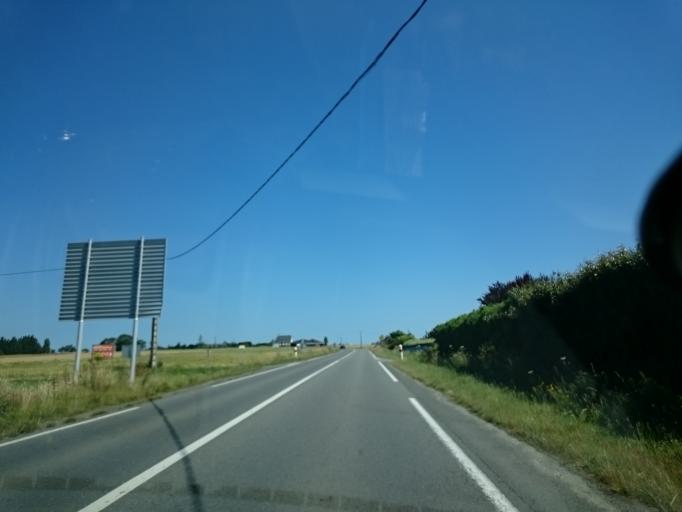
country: FR
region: Brittany
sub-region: Departement d'Ille-et-Vilaine
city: La Gouesniere
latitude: 48.6062
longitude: -1.9008
